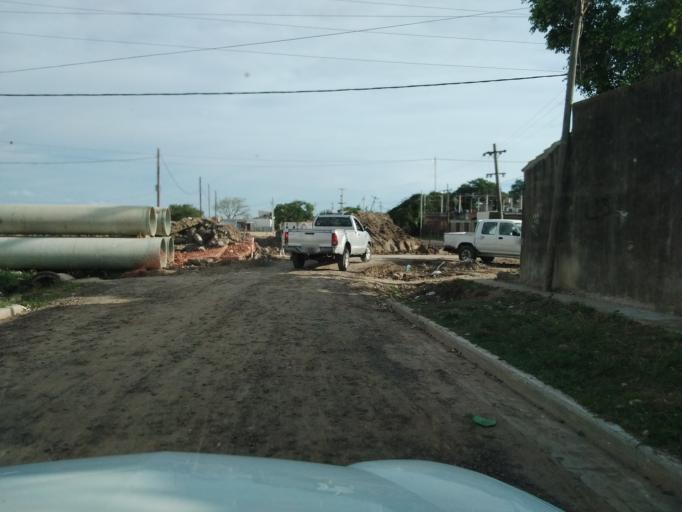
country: AR
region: Corrientes
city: Corrientes
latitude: -27.4924
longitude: -58.8455
